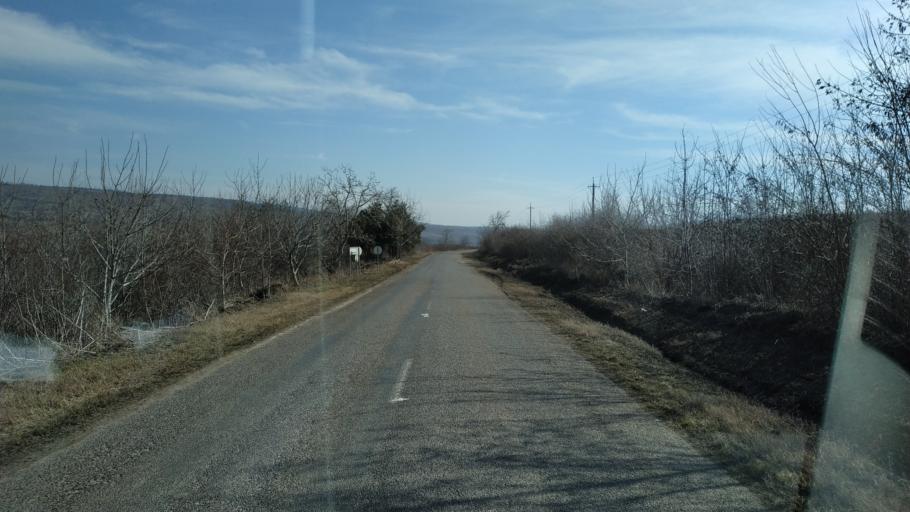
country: MD
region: Nisporeni
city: Nisporeni
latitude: 47.1780
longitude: 28.0829
